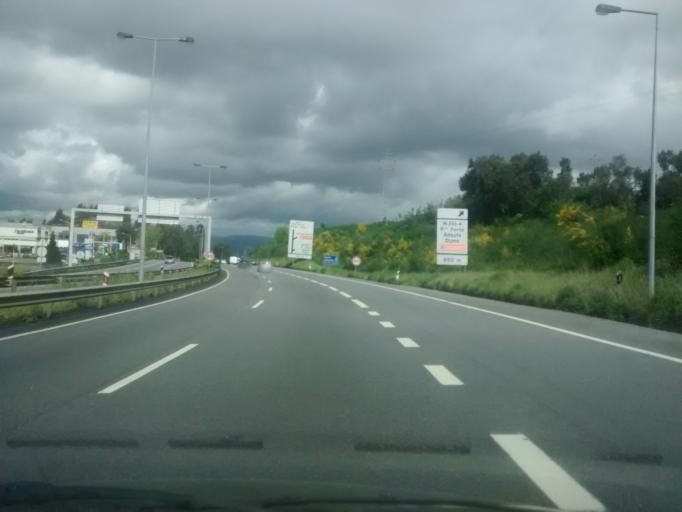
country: PT
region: Braga
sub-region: Braga
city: Braga
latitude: 41.5647
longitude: -8.4190
